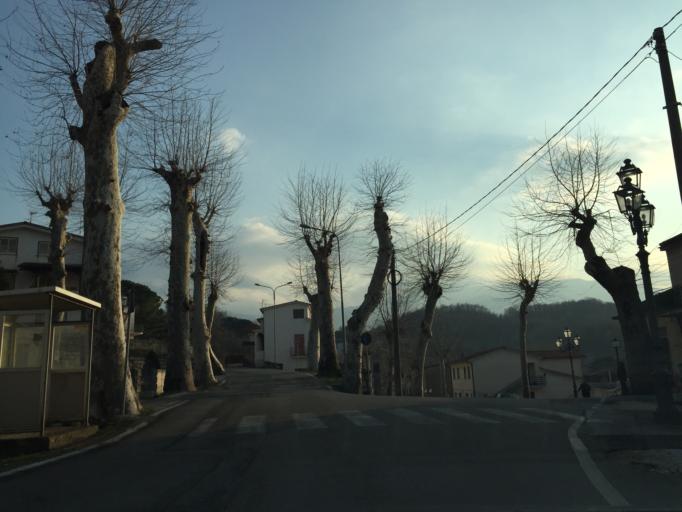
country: IT
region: Campania
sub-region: Provincia di Benevento
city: Arpaise
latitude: 41.0306
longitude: 14.7455
